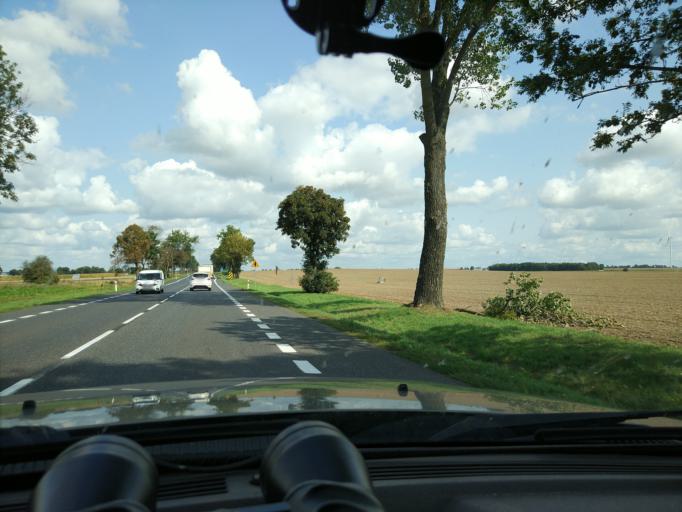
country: PL
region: Masovian Voivodeship
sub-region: Powiat mlawski
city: Wisniewo
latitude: 53.0407
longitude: 20.3408
